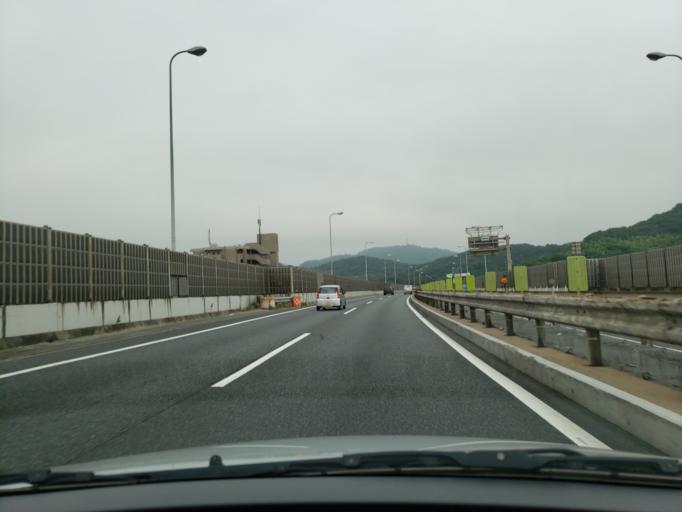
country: JP
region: Hyogo
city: Himeji
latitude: 34.8159
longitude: 134.6536
